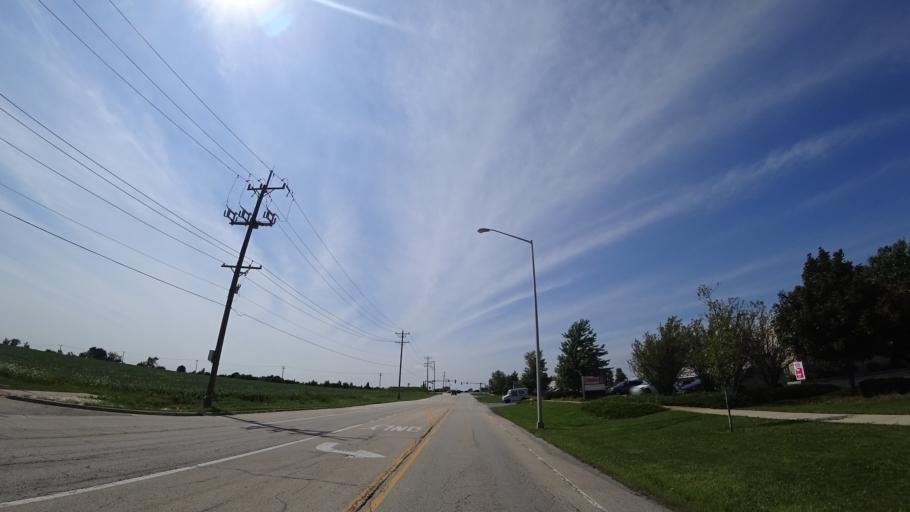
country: US
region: Illinois
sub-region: Cook County
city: Orland Hills
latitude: 41.5650
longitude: -87.8488
